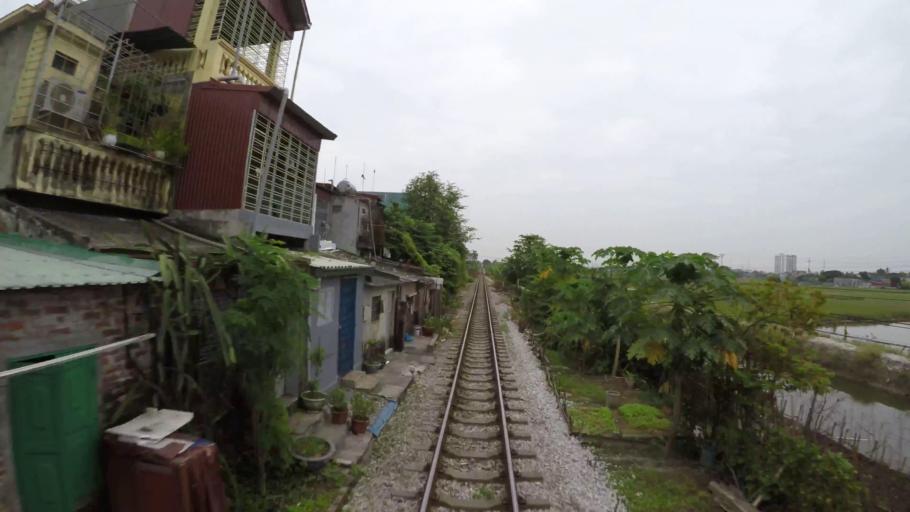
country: VN
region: Hai Phong
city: An Duong
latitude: 20.8962
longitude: 106.5850
